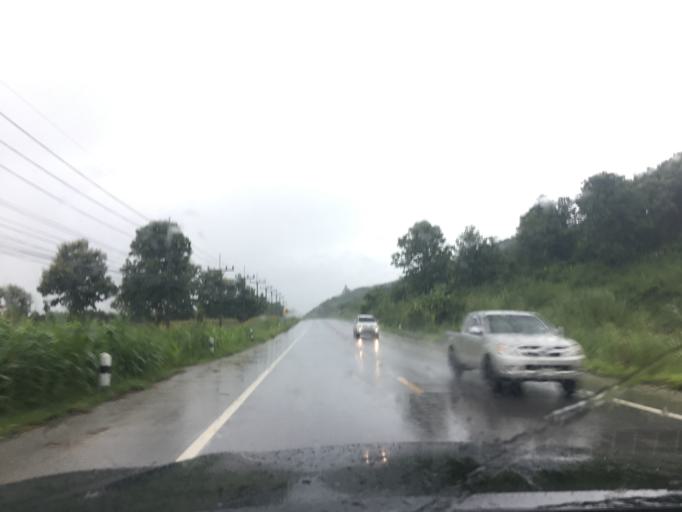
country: TH
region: Chiang Rai
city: Chiang Saen
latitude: 20.2690
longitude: 100.1939
